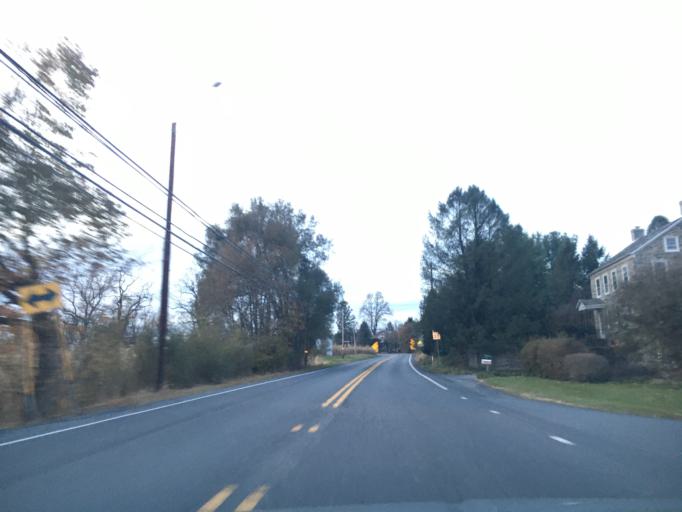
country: US
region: Pennsylvania
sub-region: Lehigh County
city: Stiles
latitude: 40.6485
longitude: -75.5342
